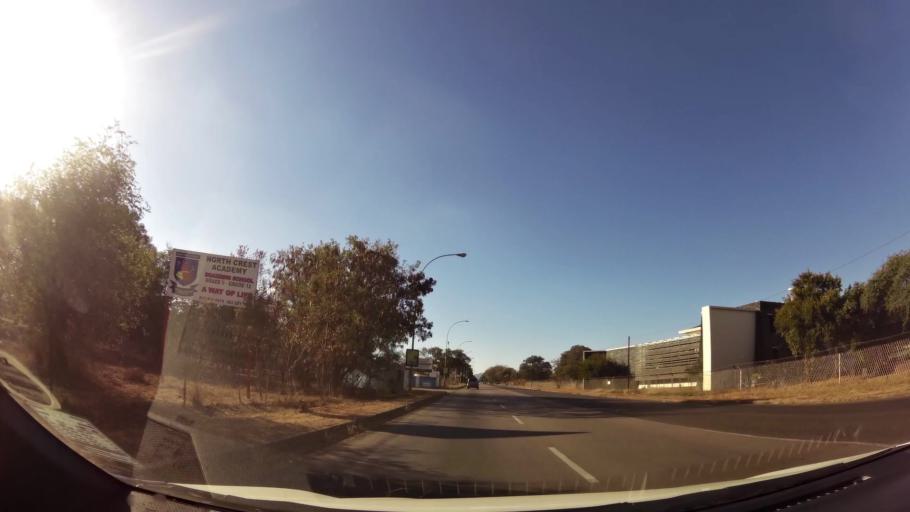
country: ZA
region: Limpopo
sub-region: Waterberg District Municipality
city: Mokopane
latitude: -24.1986
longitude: 29.0074
